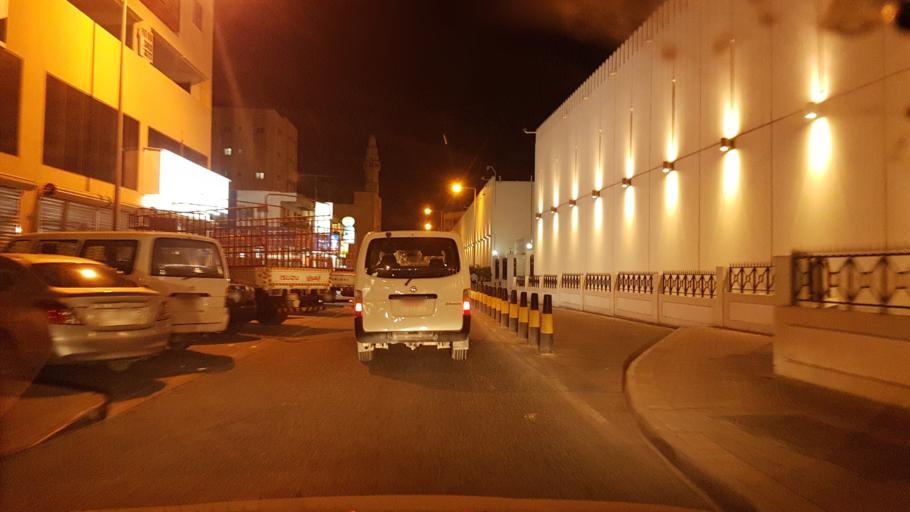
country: BH
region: Manama
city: Manama
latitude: 26.2224
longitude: 50.5728
